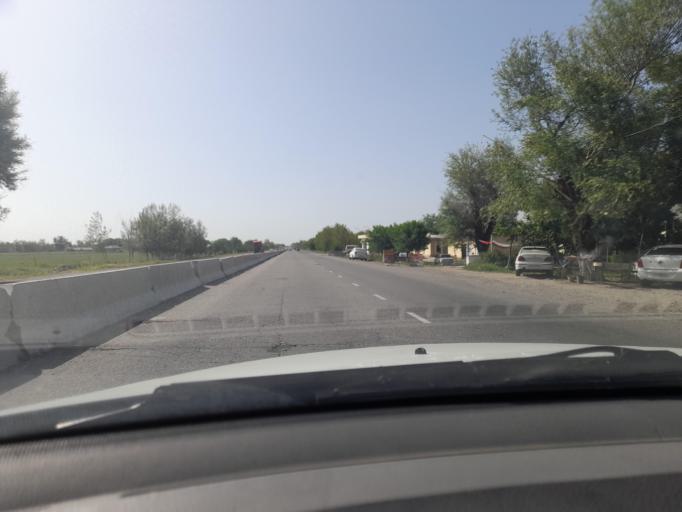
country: UZ
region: Samarqand
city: Chelak
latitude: 39.8460
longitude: 66.8096
